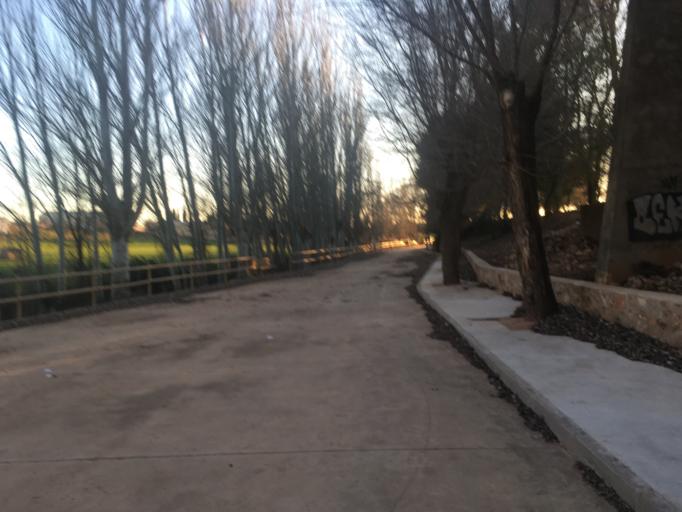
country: ES
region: Castille-La Mancha
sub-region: Provincia de Cuenca
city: Atalaya del Canavate
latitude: 39.5540
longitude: -2.2517
